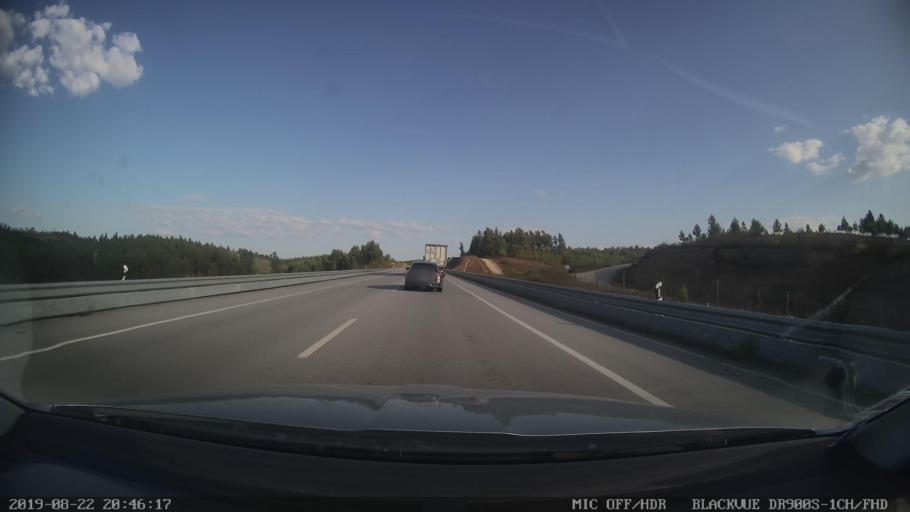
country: PT
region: Castelo Branco
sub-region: Proenca-A-Nova
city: Proenca-a-Nova
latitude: 39.7251
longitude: -7.8749
